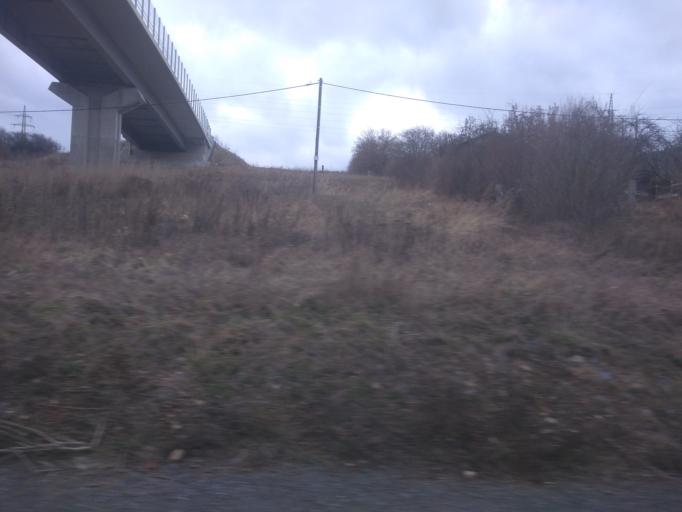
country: CZ
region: Plzensky
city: Vejprnice
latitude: 49.7379
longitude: 13.3143
